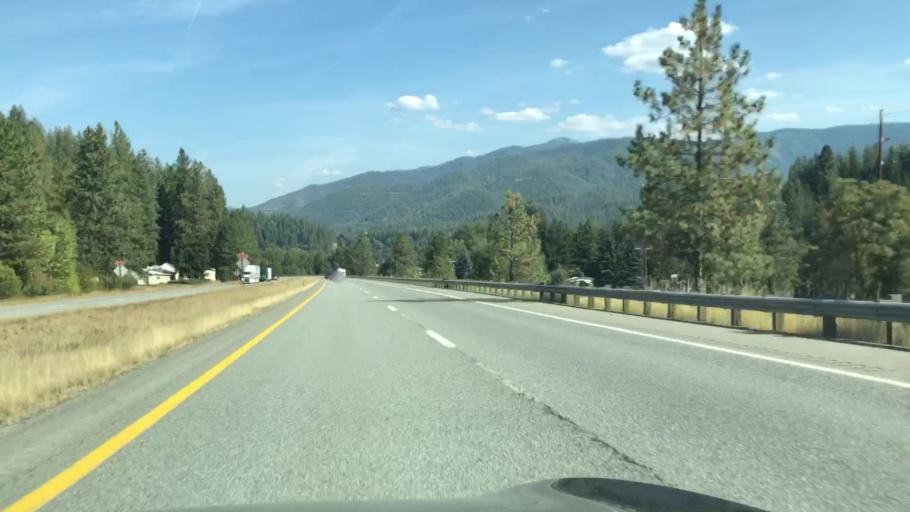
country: US
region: Idaho
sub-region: Shoshone County
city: Pinehurst
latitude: 47.5442
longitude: -116.2473
